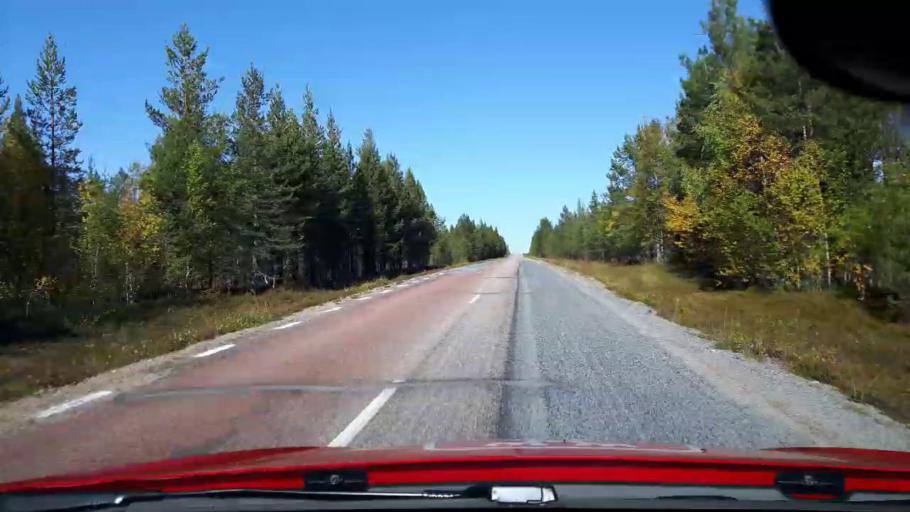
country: SE
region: Jaemtland
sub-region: Harjedalens Kommun
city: Sveg
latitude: 61.7238
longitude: 14.1670
